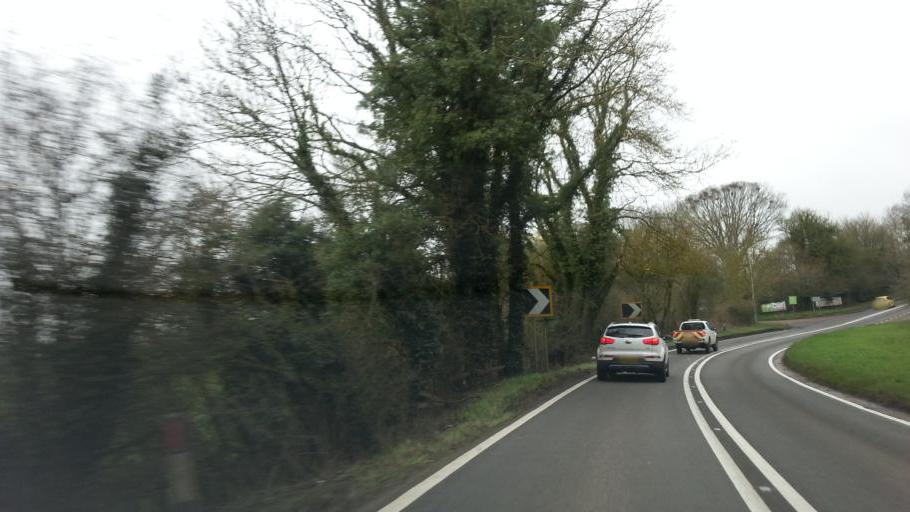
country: GB
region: England
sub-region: Oxfordshire
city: Adderbury
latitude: 52.0591
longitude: -1.2374
